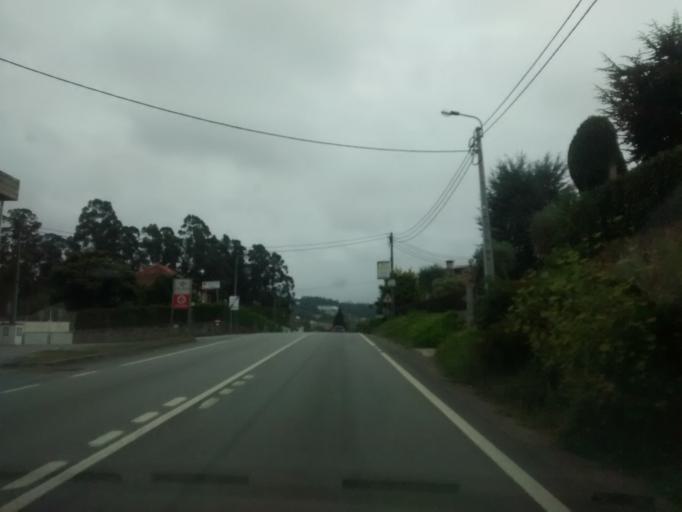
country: PT
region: Braga
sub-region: Braga
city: Oliveira
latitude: 41.4767
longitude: -8.4836
